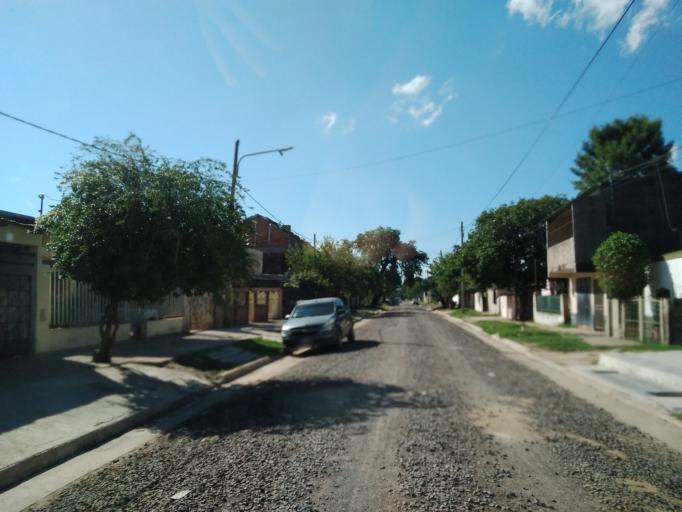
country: AR
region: Corrientes
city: Corrientes
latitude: -27.4847
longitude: -58.8107
